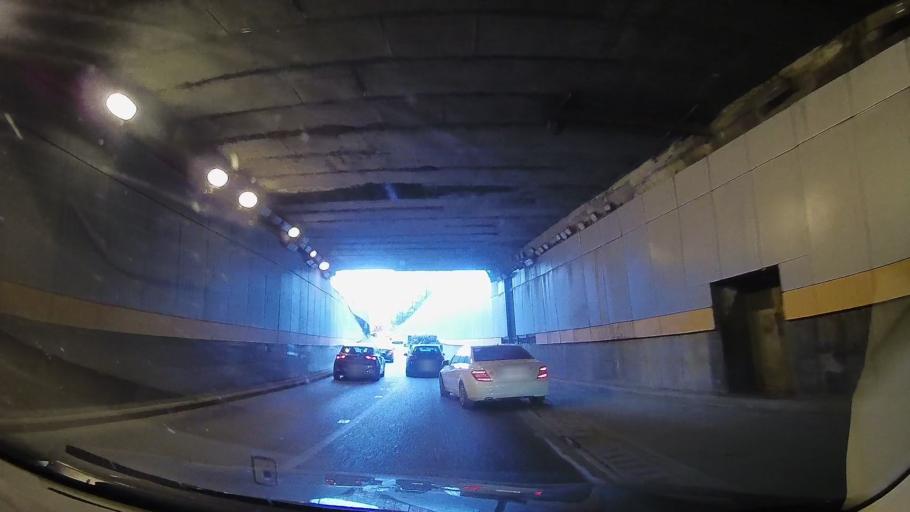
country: RO
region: Bucuresti
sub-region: Municipiul Bucuresti
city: Bucharest
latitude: 44.4461
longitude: 26.1237
